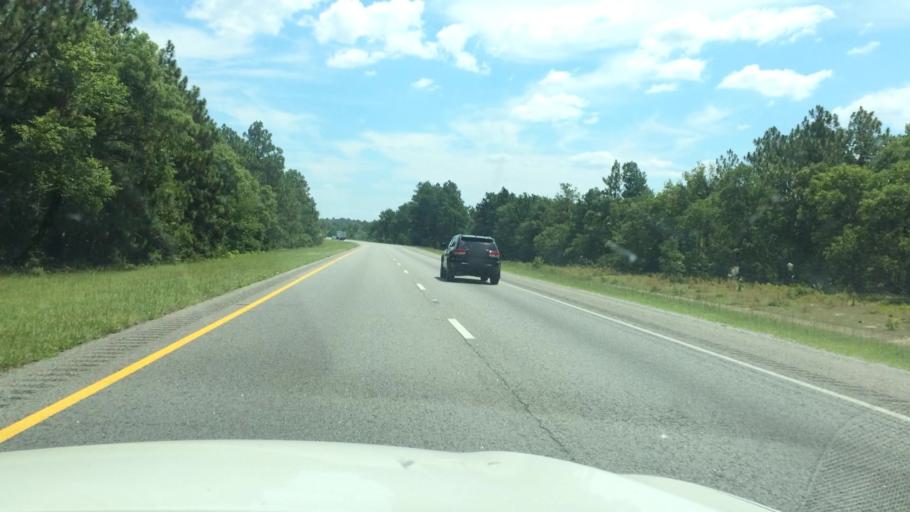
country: US
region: South Carolina
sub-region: Aiken County
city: Aiken
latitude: 33.7077
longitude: -81.5890
